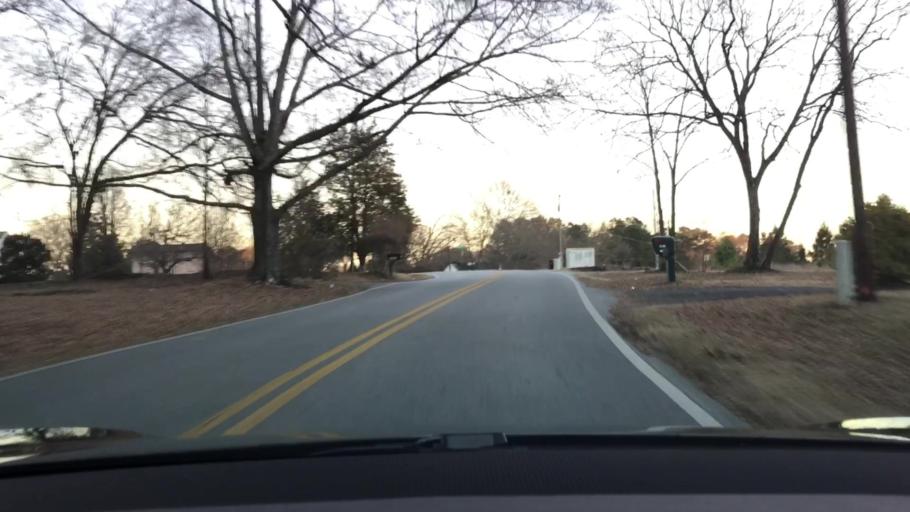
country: US
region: Georgia
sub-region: Gwinnett County
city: Grayson
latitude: 33.8871
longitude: -83.9162
